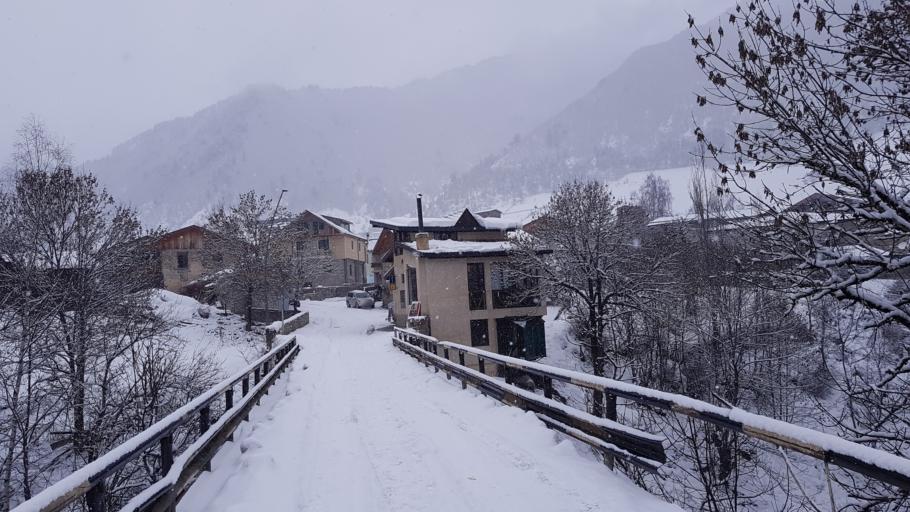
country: GE
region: Samegrelo and Zemo Svaneti
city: Mest'ia
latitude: 43.0425
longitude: 42.7280
